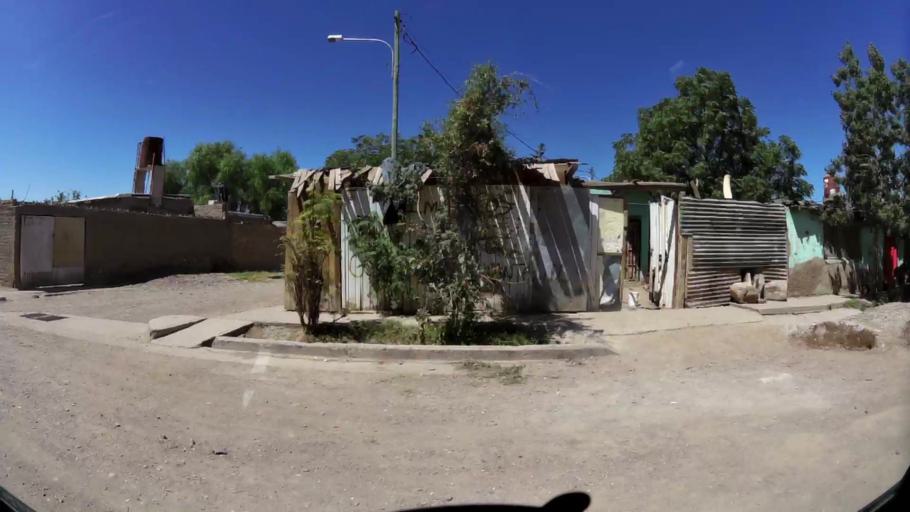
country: AR
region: Mendoza
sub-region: Departamento de Godoy Cruz
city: Godoy Cruz
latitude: -32.9303
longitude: -68.8703
